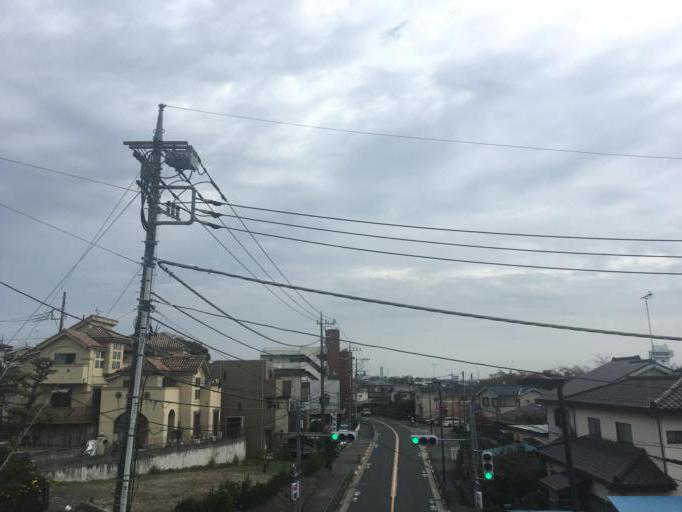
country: JP
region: Tokyo
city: Hino
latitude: 35.6991
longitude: 139.3632
